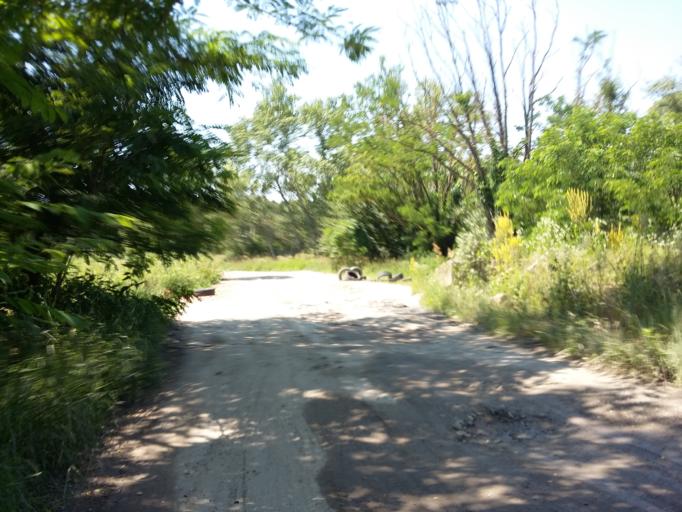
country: AT
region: Lower Austria
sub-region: Politischer Bezirk Ganserndorf
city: Marchegg
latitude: 48.2780
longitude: 16.9668
